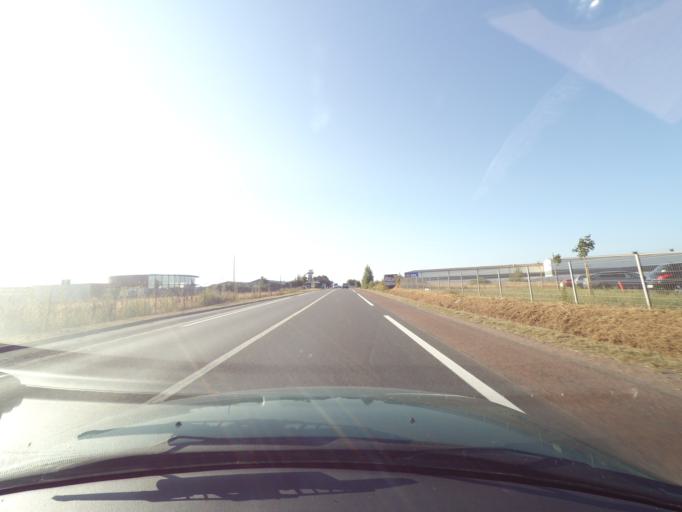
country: FR
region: Poitou-Charentes
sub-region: Departement des Deux-Sevres
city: Parthenay
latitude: 46.6685
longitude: -0.2546
